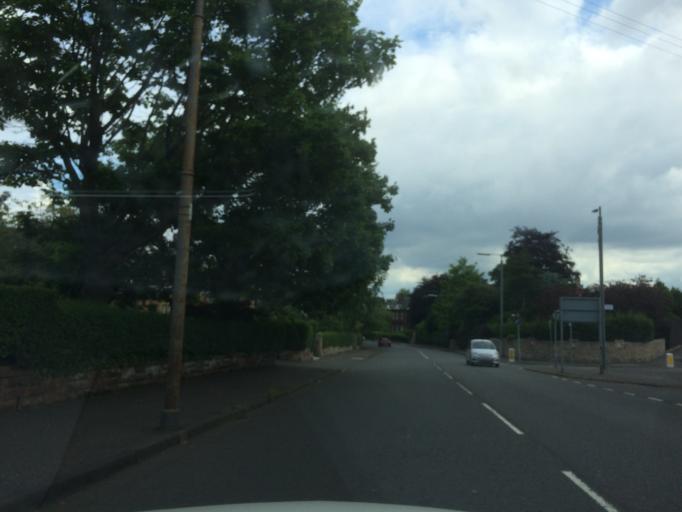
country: GB
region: Scotland
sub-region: East Renfrewshire
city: Giffnock
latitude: 55.8122
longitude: -4.2791
